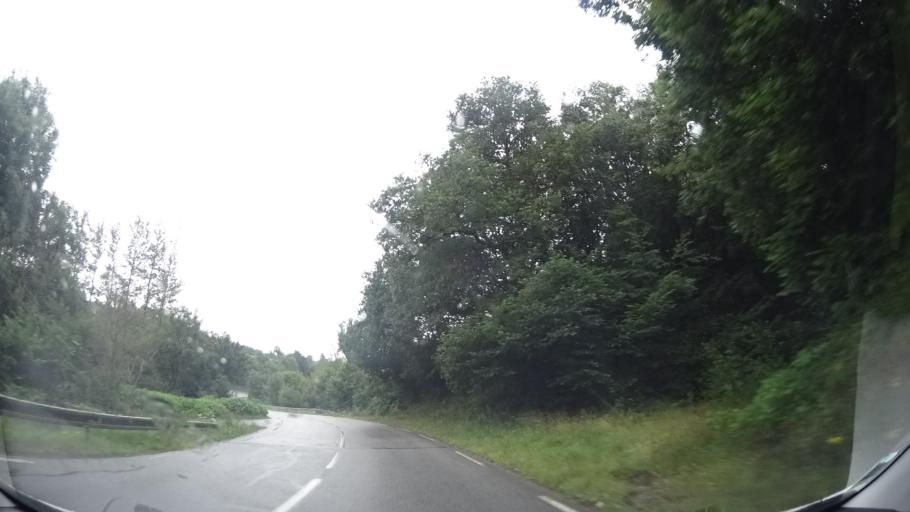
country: FR
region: Lower Normandy
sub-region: Departement de la Manche
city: Beaumont-Hague
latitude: 49.6122
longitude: -1.7896
